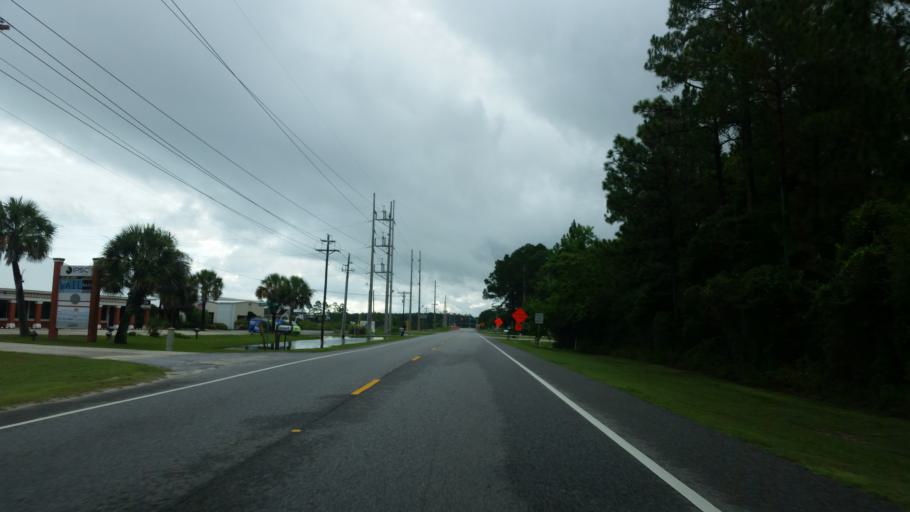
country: US
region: Alabama
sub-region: Baldwin County
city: Orange Beach
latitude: 30.2882
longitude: -87.6390
